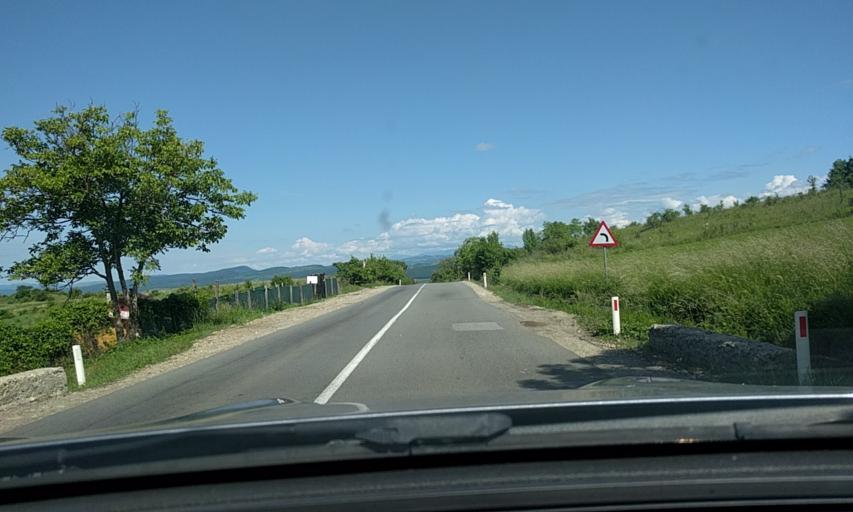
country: RO
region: Bistrita-Nasaud
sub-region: Comuna Dumitra
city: Dumitra
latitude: 47.1979
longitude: 24.4833
